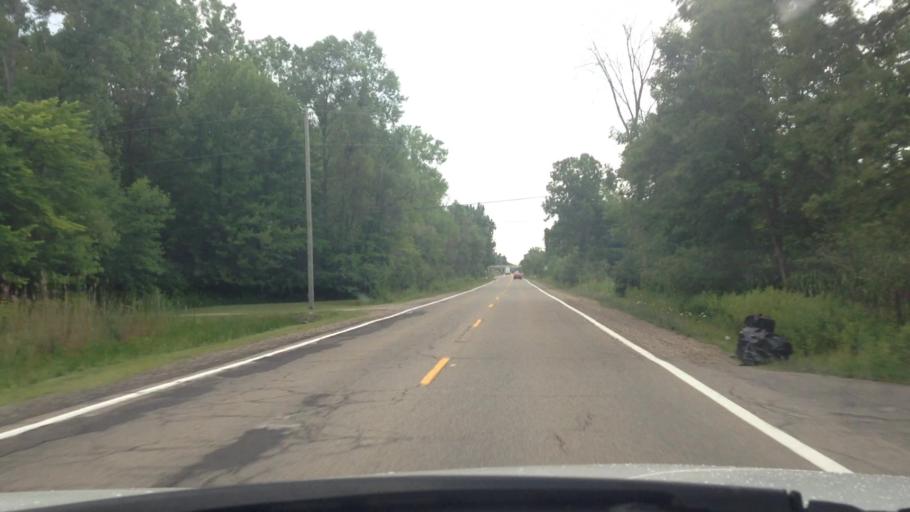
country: US
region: Michigan
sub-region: Oakland County
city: Clarkston
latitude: 42.7277
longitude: -83.3497
